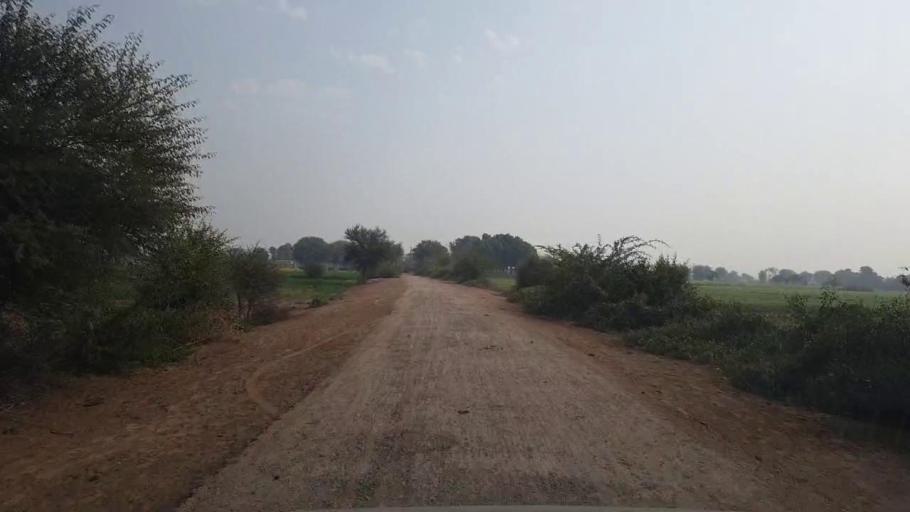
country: PK
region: Sindh
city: Hala
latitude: 25.7626
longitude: 68.4311
